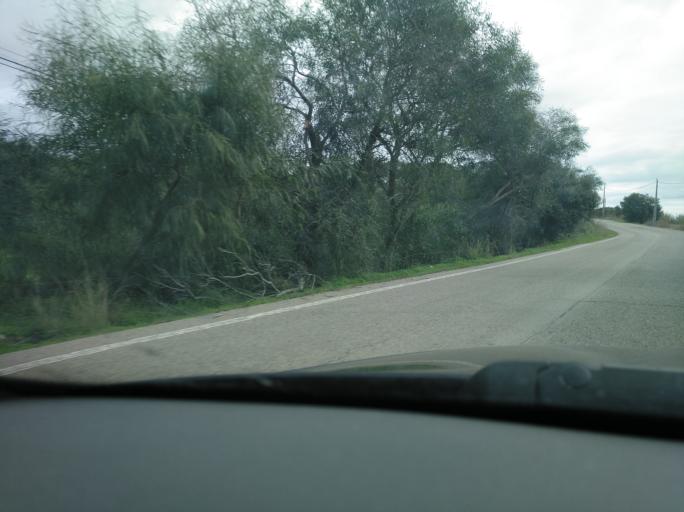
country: PT
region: Faro
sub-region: Castro Marim
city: Castro Marim
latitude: 37.2220
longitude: -7.4803
